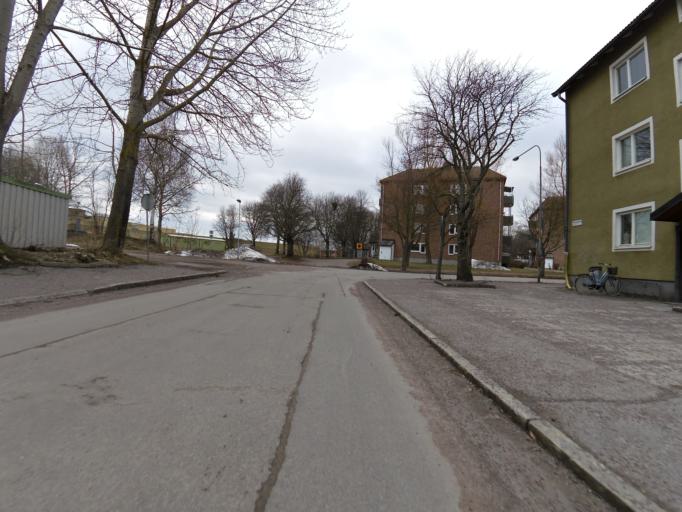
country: SE
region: Gaevleborg
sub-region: Gavle Kommun
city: Gavle
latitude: 60.6693
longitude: 17.1703
